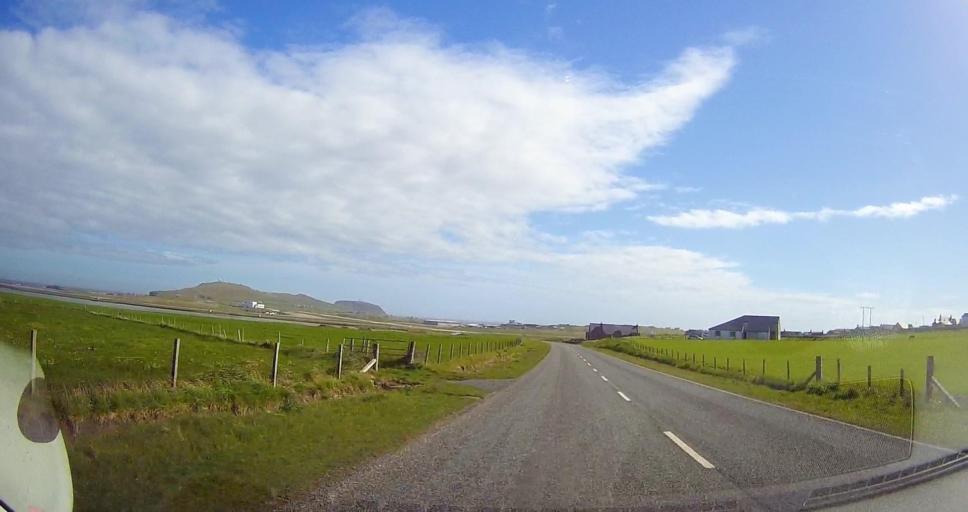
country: GB
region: Scotland
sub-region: Shetland Islands
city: Sandwick
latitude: 59.8893
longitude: -1.3033
